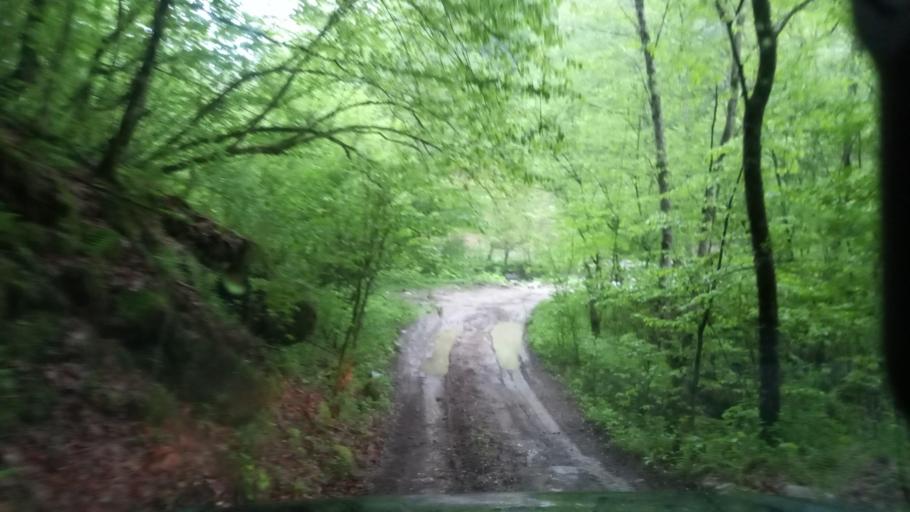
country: RU
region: Kabardino-Balkariya
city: Belaya Rechka
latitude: 43.3967
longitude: 43.4436
